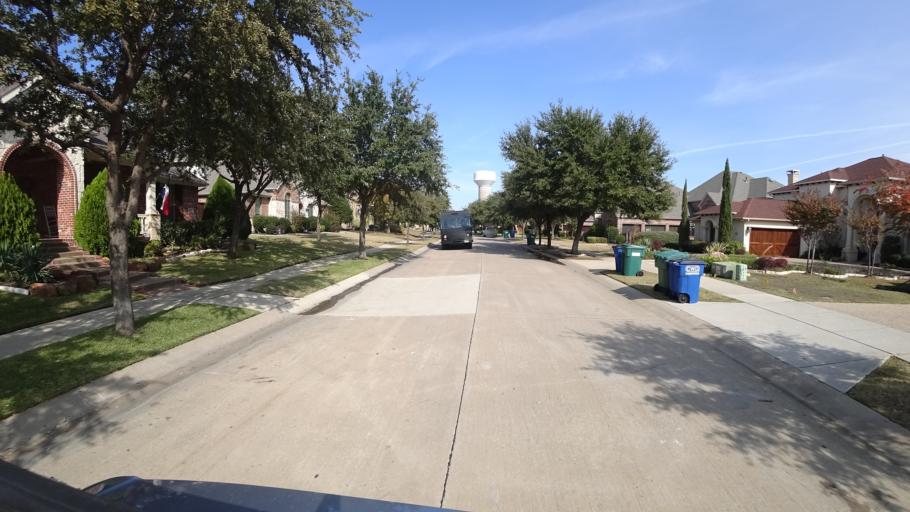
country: US
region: Texas
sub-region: Denton County
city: The Colony
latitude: 33.0410
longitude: -96.9113
